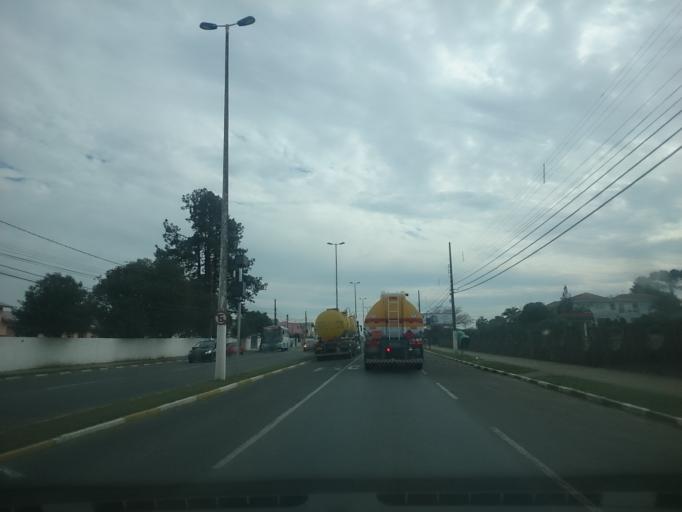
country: BR
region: Santa Catarina
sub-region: Lages
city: Lages
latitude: -27.7936
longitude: -50.3066
